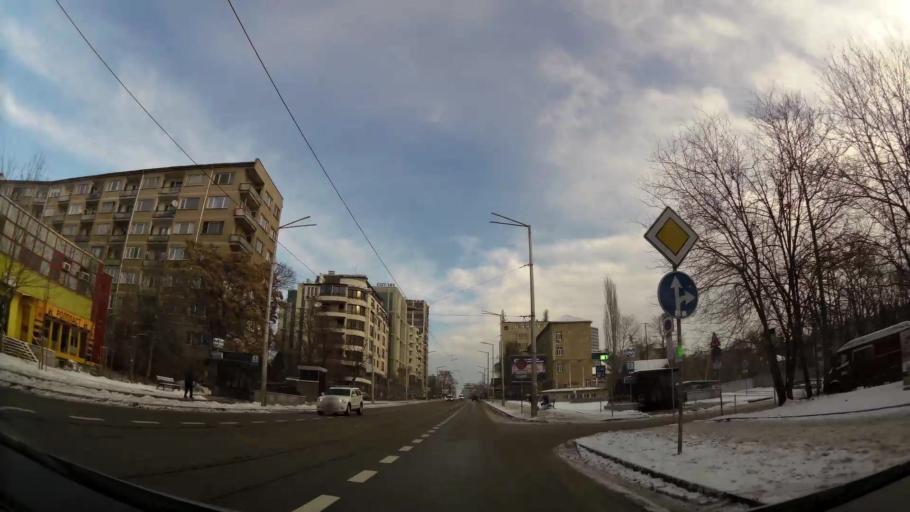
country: BG
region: Sofia-Capital
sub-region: Stolichna Obshtina
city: Sofia
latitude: 42.6692
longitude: 23.3196
